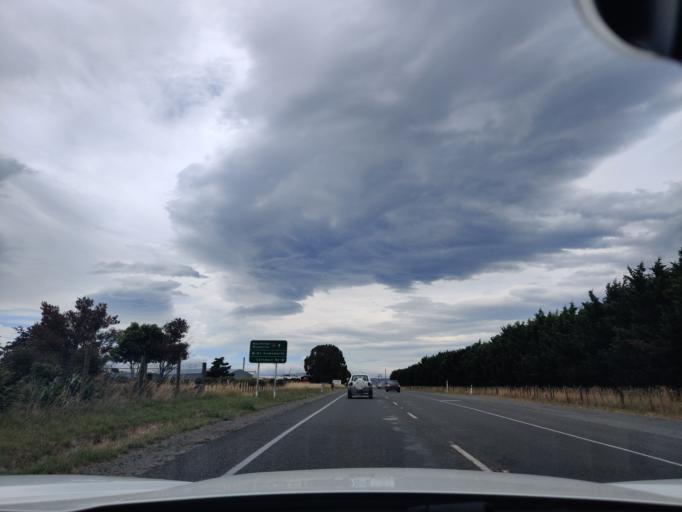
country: NZ
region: Wellington
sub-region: Masterton District
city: Masterton
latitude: -40.9722
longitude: 175.5988
